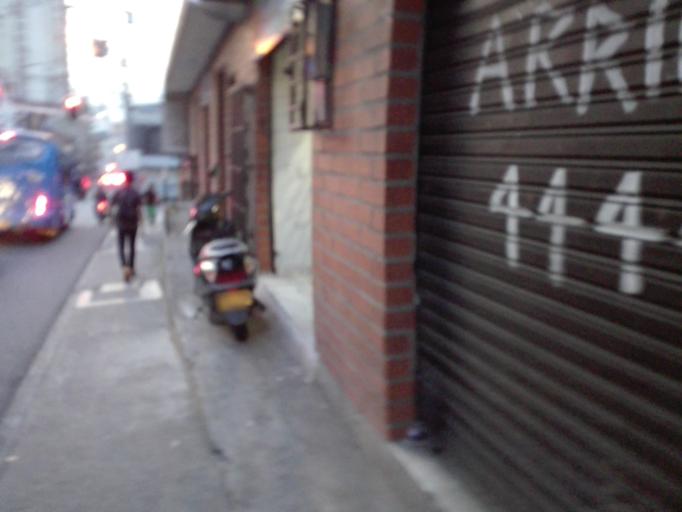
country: CO
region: Antioquia
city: Medellin
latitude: 6.2434
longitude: -75.5645
